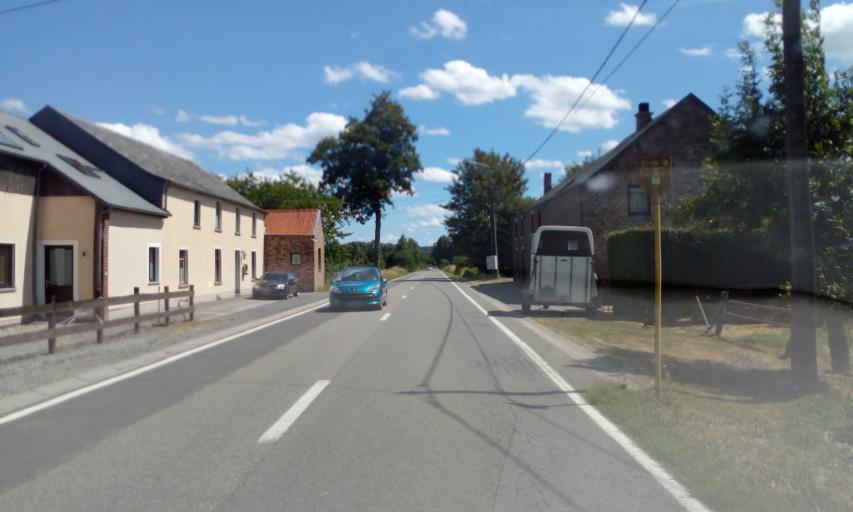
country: BE
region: Wallonia
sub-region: Province de Namur
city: Beauraing
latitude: 50.1200
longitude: 4.9266
